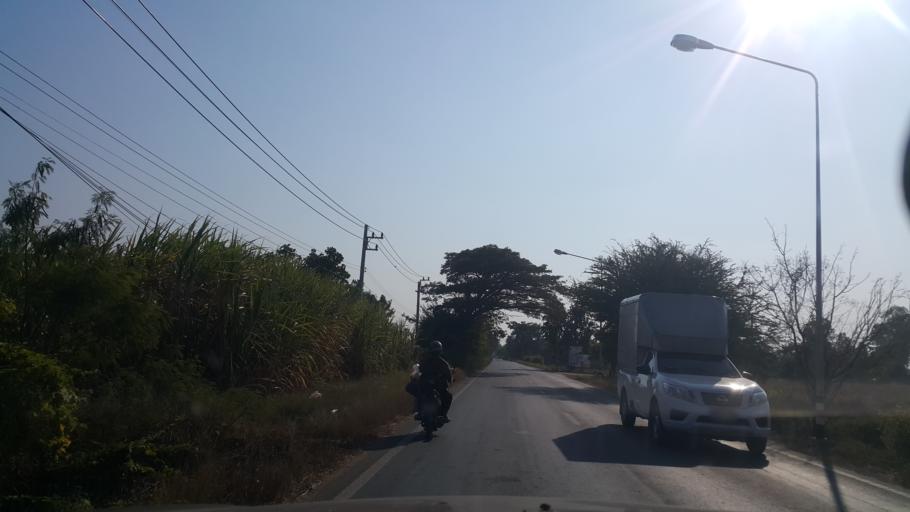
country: TH
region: Nakhon Ratchasima
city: Phimai
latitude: 15.1772
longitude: 102.4048
